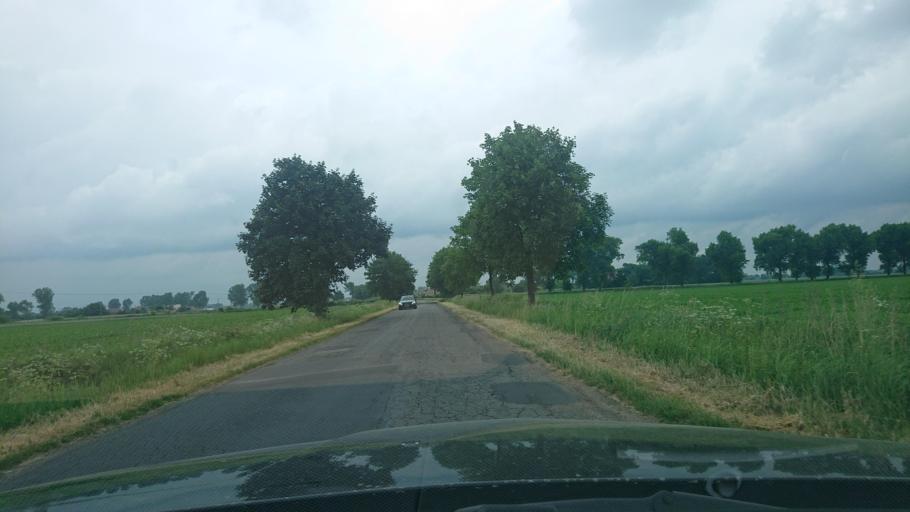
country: PL
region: Greater Poland Voivodeship
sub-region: Powiat gnieznienski
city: Czerniejewo
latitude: 52.4652
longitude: 17.5217
